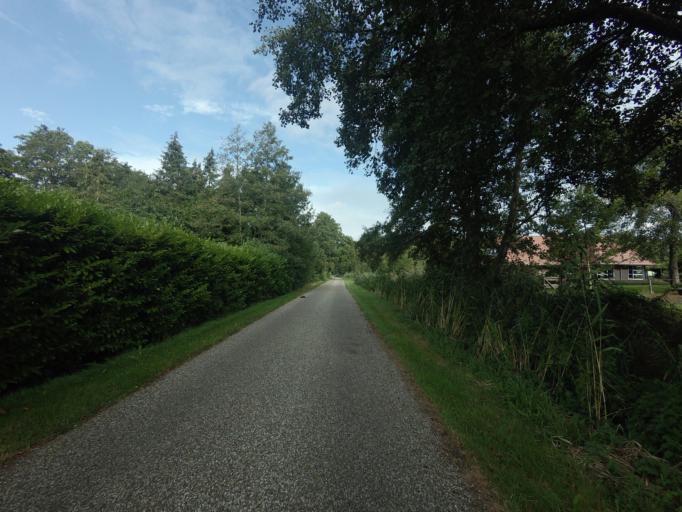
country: NL
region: Friesland
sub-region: Gemeente Heerenveen
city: Jubbega
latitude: 52.9872
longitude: 6.1142
